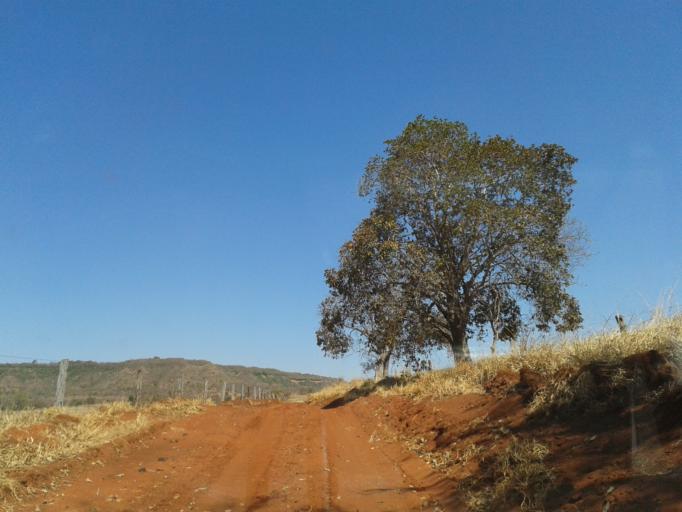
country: BR
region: Minas Gerais
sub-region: Santa Vitoria
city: Santa Vitoria
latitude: -19.0703
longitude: -50.0572
